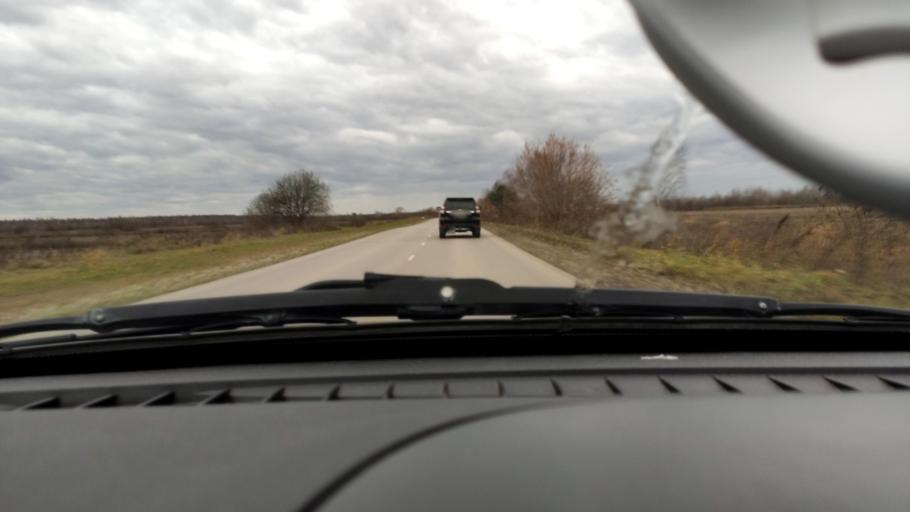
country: RU
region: Perm
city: Kondratovo
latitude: 57.9974
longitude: 56.0821
